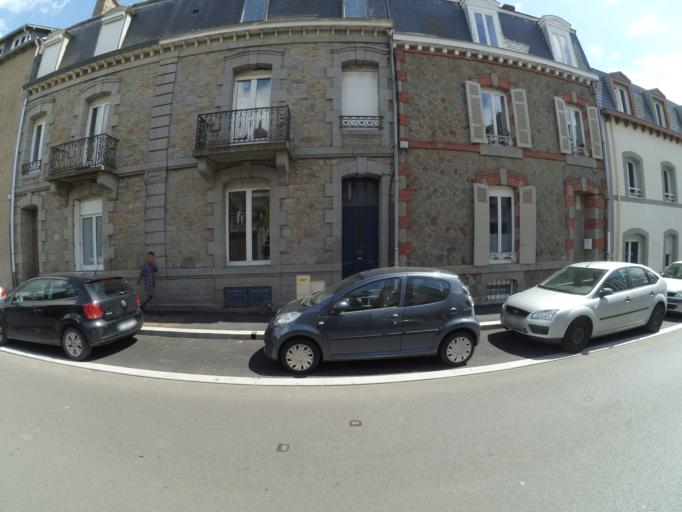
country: FR
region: Brittany
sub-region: Departement des Cotes-d'Armor
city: Saint-Brieuc
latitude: 48.5076
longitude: -2.7720
